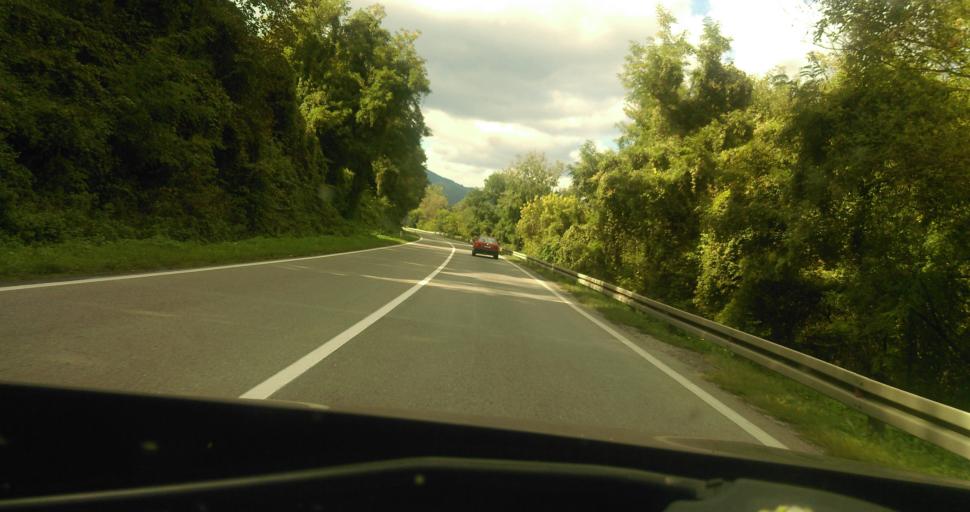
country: RS
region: Central Serbia
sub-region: Moravicki Okrug
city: Cacak
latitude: 43.8985
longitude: 20.2780
